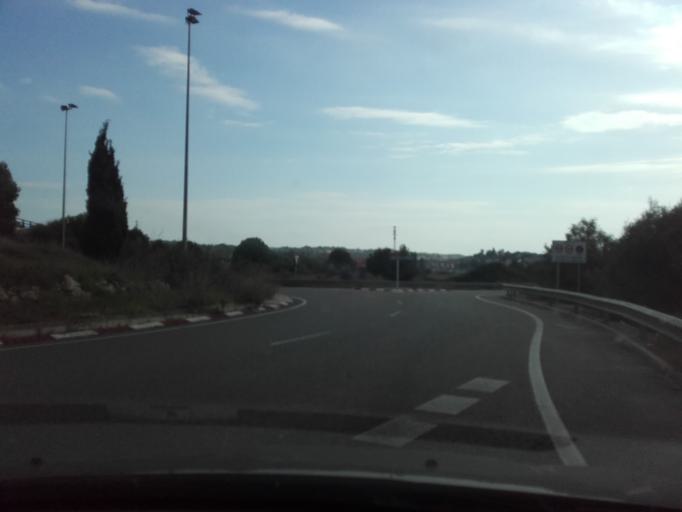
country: ES
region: Catalonia
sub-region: Provincia de Tarragona
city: El Vendrell
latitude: 41.2304
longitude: 1.5402
